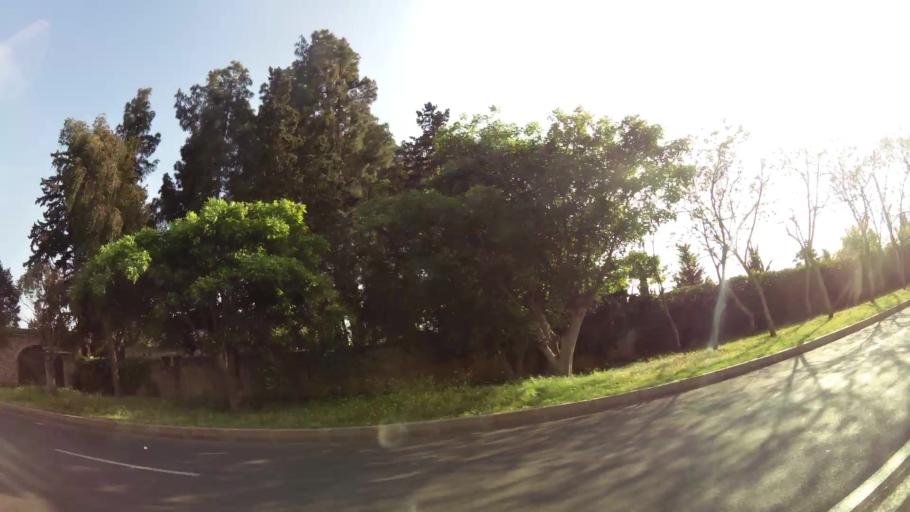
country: MA
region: Rabat-Sale-Zemmour-Zaer
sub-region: Rabat
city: Rabat
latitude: 33.9372
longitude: -6.8179
